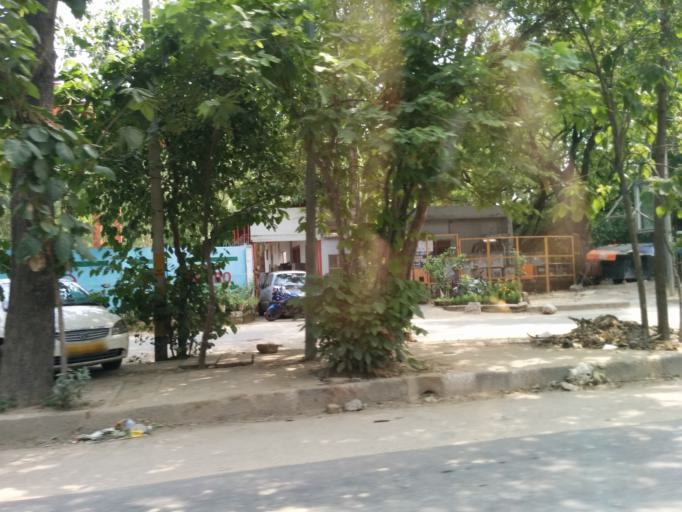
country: IN
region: NCT
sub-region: New Delhi
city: New Delhi
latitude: 28.5463
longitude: 77.1956
